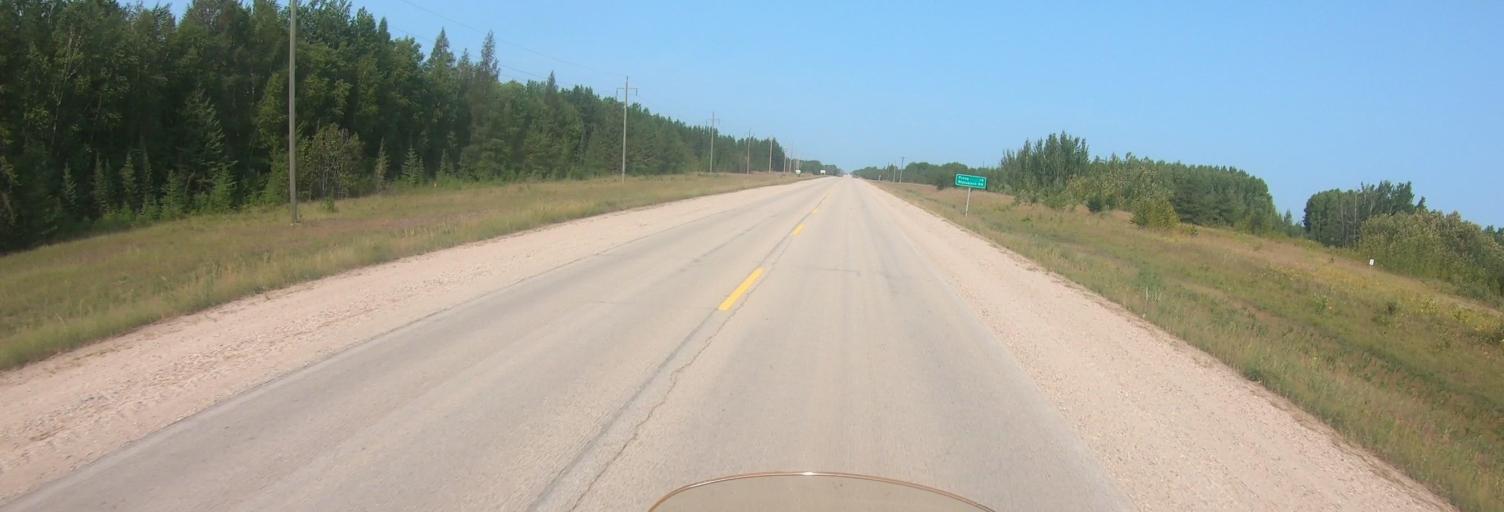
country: US
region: Minnesota
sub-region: Roseau County
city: Roseau
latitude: 49.0387
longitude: -95.7729
